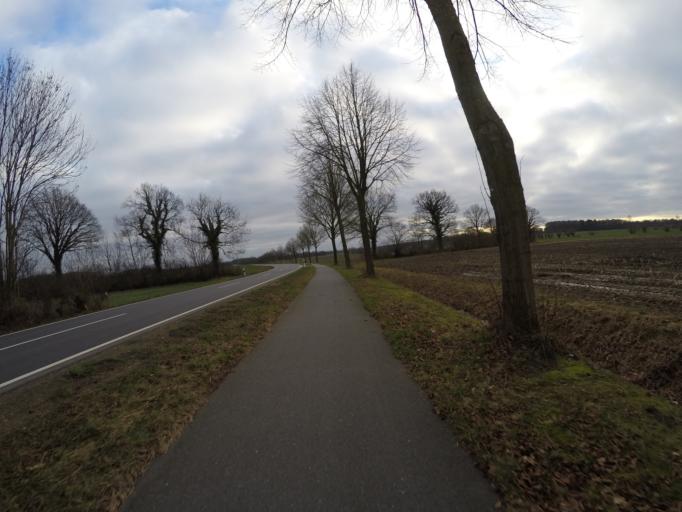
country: DE
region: Schleswig-Holstein
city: Alveslohe
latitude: 53.7745
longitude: 9.9062
